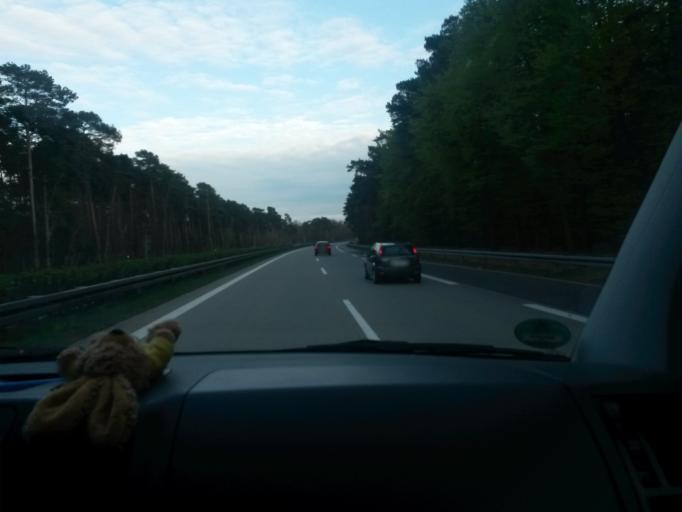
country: DE
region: Brandenburg
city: Lubbenau
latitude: 51.8264
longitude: 14.0015
